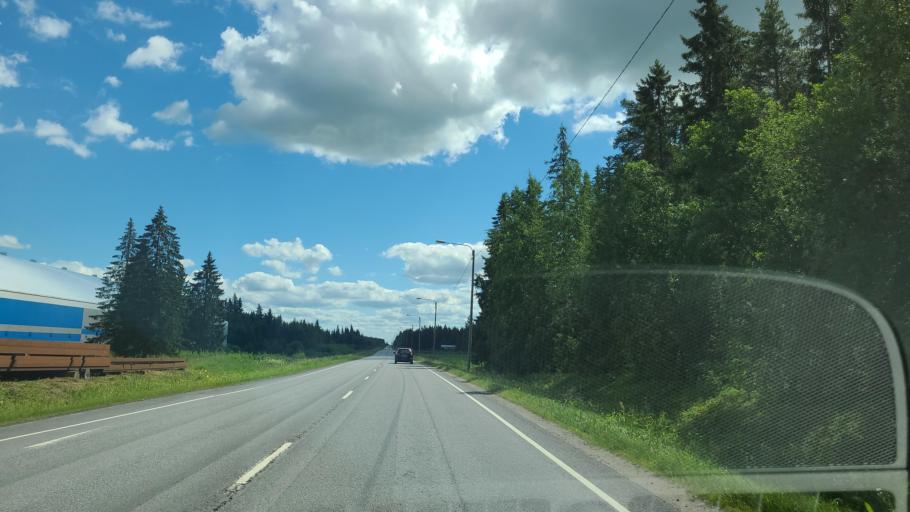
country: FI
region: Southern Ostrobothnia
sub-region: Seinaejoki
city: Ylistaro
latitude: 62.8874
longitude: 22.6543
